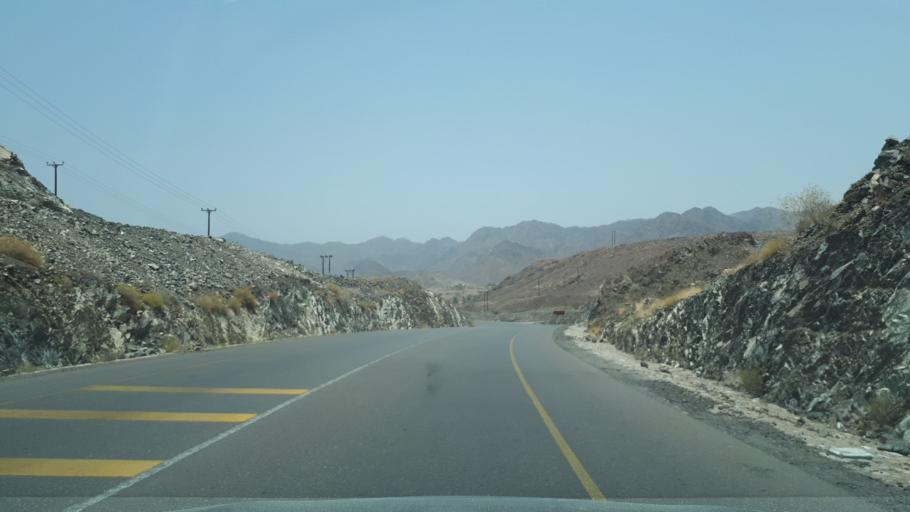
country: OM
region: Al Batinah
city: Rustaq
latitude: 23.4167
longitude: 57.3017
